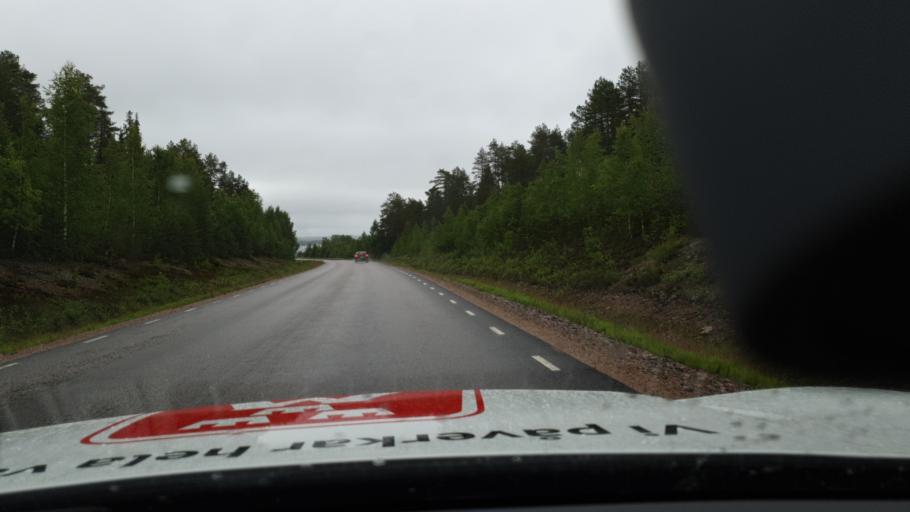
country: SE
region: Norrbotten
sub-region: Overtornea Kommun
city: OEvertornea
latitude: 66.5281
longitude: 23.7743
